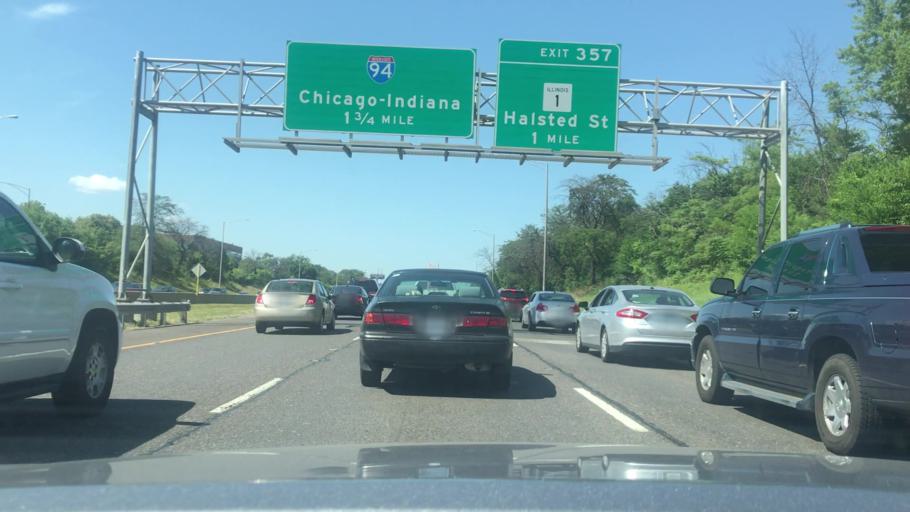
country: US
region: Illinois
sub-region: Cook County
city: Calumet Park
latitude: 41.7033
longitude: -87.6528
